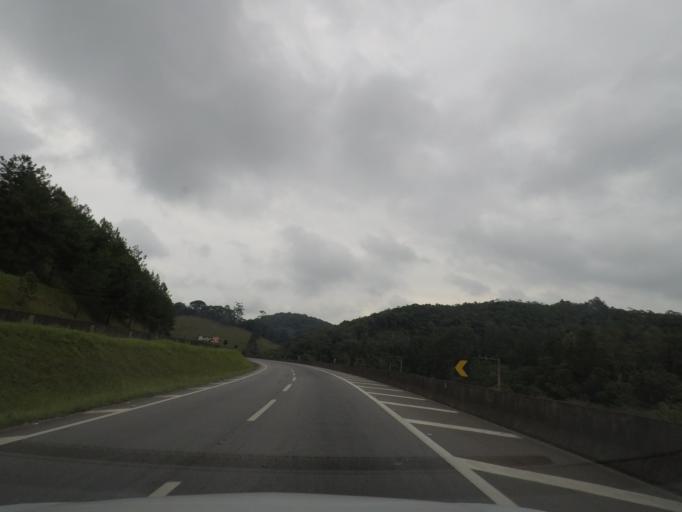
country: BR
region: Sao Paulo
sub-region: Juquitiba
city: Juquitiba
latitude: -24.0030
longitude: -47.1564
